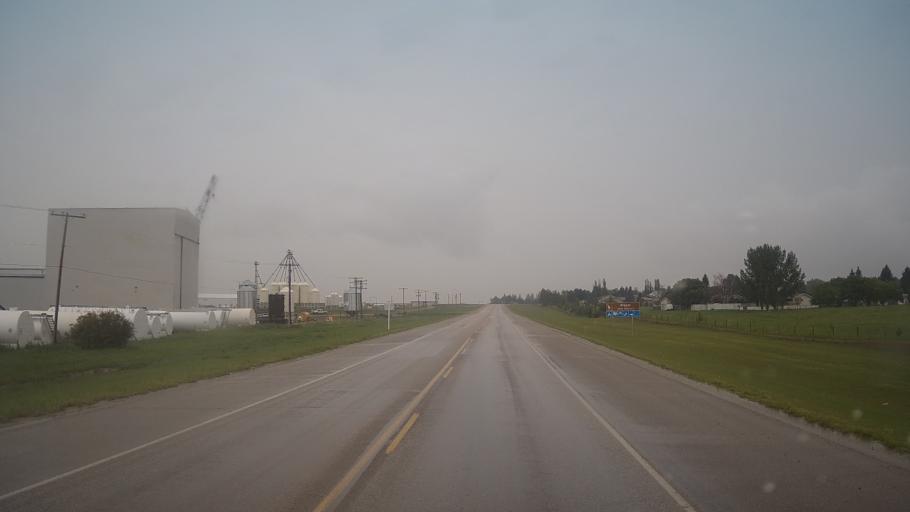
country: CA
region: Saskatchewan
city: Biggar
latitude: 52.0594
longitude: -107.9997
